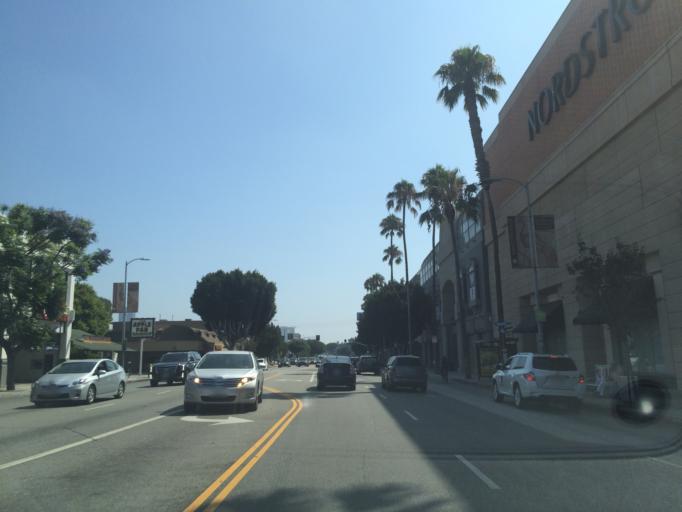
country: US
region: California
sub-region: Los Angeles County
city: Westwood, Los Angeles
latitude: 34.0403
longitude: -118.4281
